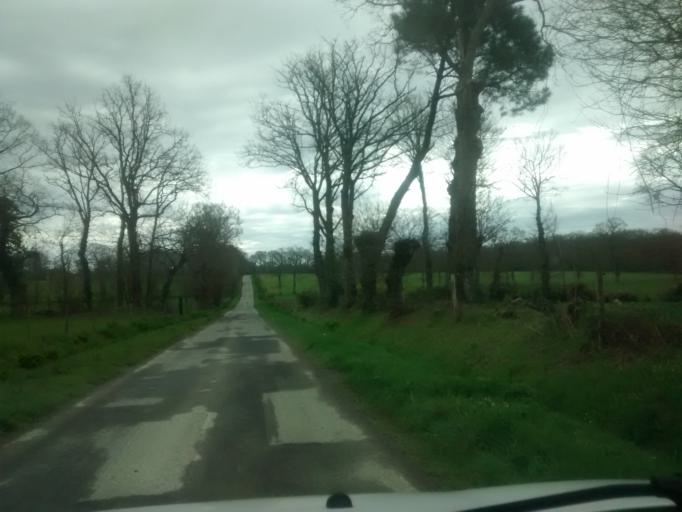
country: FR
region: Brittany
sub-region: Departement d'Ille-et-Vilaine
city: Betton
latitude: 48.1690
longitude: -1.6152
